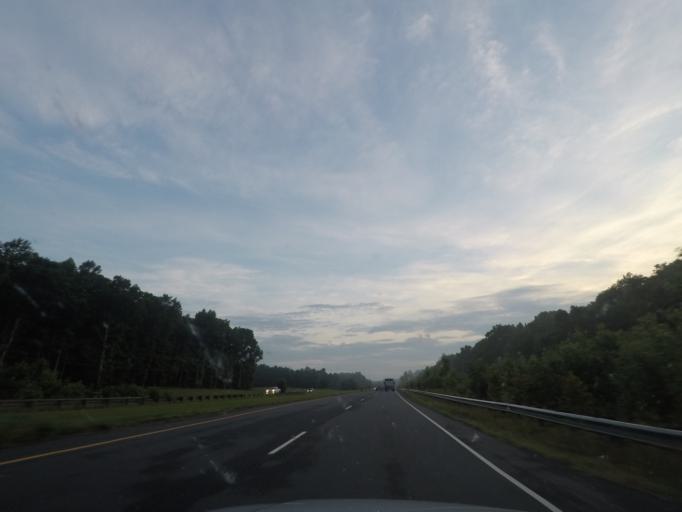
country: US
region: North Carolina
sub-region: Person County
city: Roxboro
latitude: 36.2570
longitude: -78.9440
